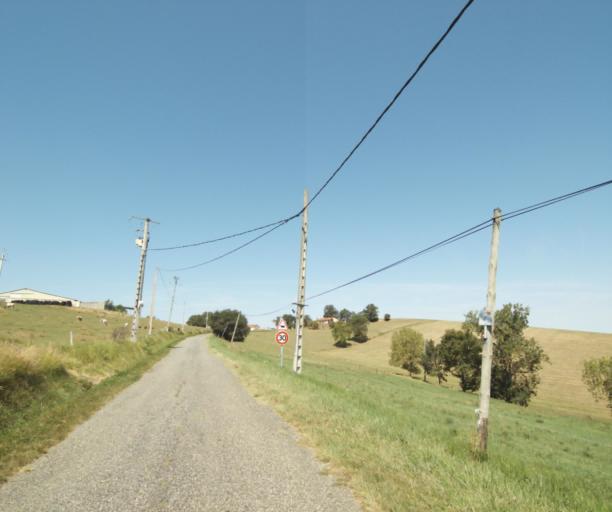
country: FR
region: Midi-Pyrenees
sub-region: Departement de l'Ariege
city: Lezat-sur-Leze
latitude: 43.2760
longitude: 1.3745
